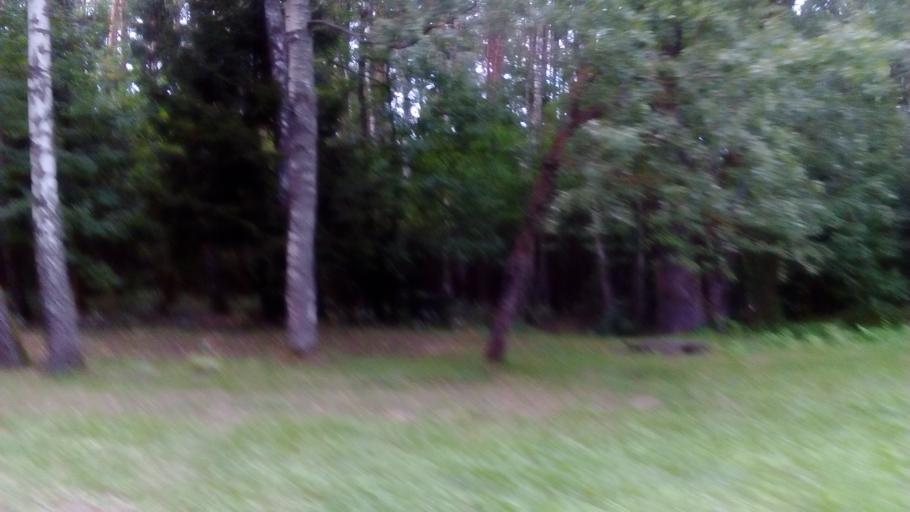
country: LT
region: Alytaus apskritis
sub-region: Alytus
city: Alytus
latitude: 54.3933
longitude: 24.0768
